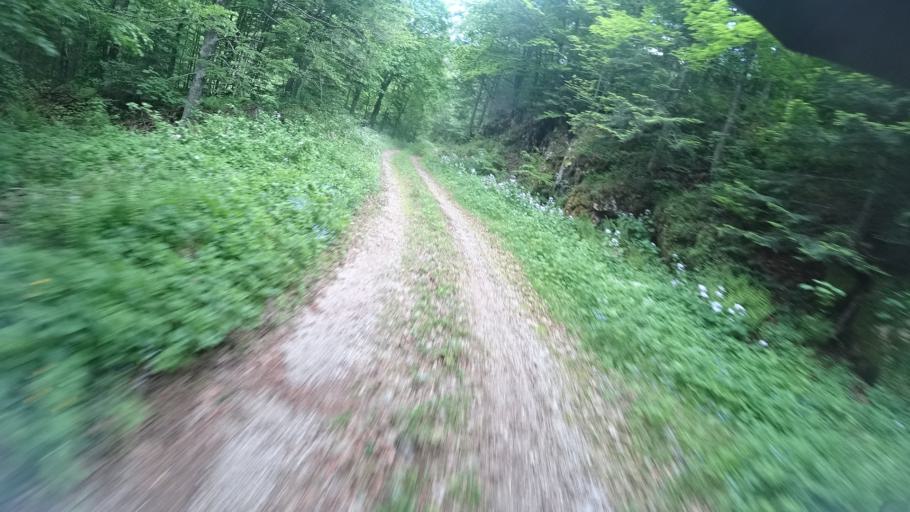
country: HR
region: Zadarska
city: Gracac
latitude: 44.4765
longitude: 15.8863
